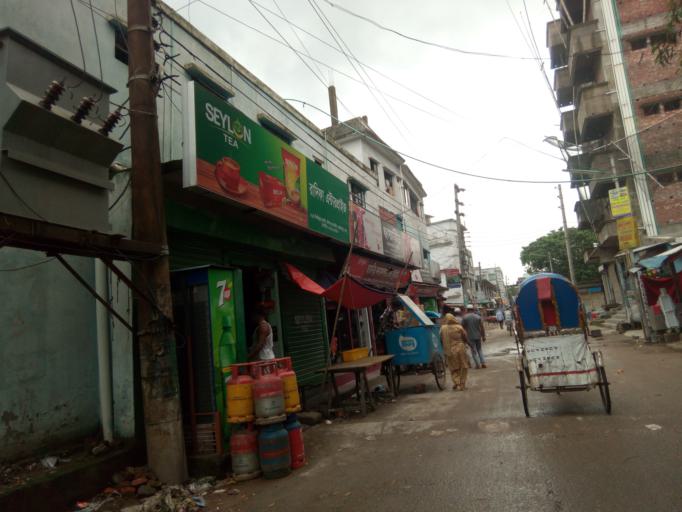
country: BD
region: Dhaka
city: Azimpur
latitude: 23.7489
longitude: 90.3433
